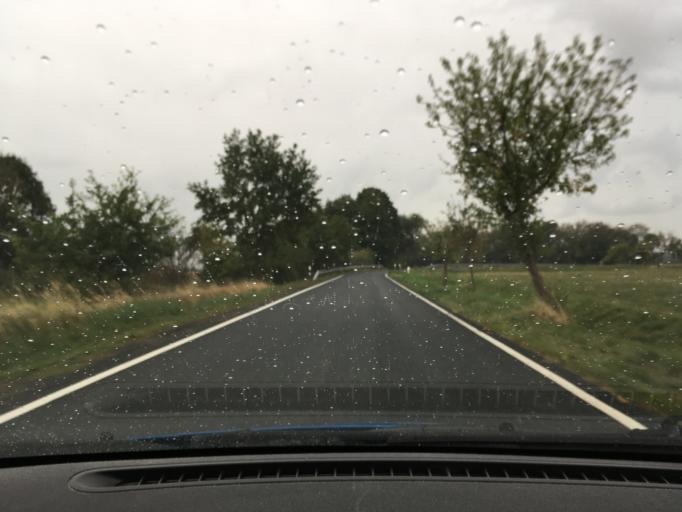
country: DE
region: Lower Saxony
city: Hitzacker
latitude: 53.1898
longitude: 11.0372
